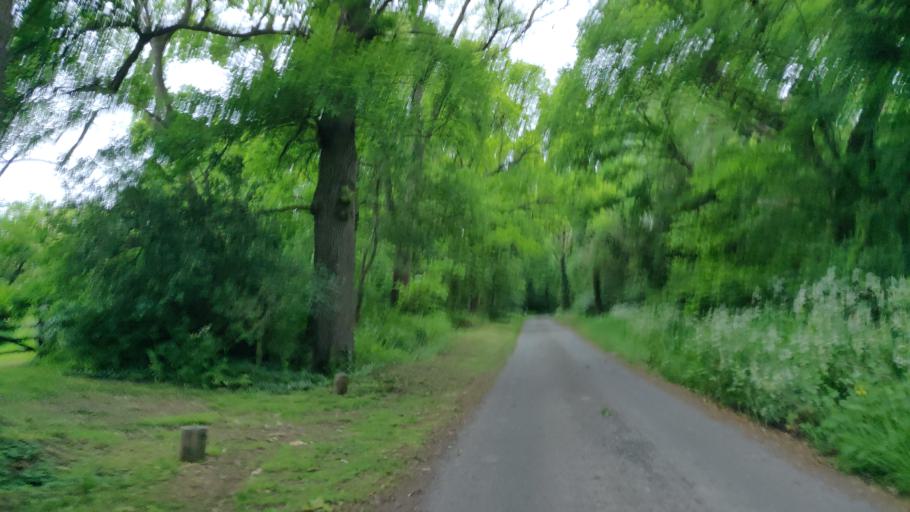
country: GB
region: England
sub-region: West Sussex
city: Southwater
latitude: 51.0158
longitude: -0.3327
